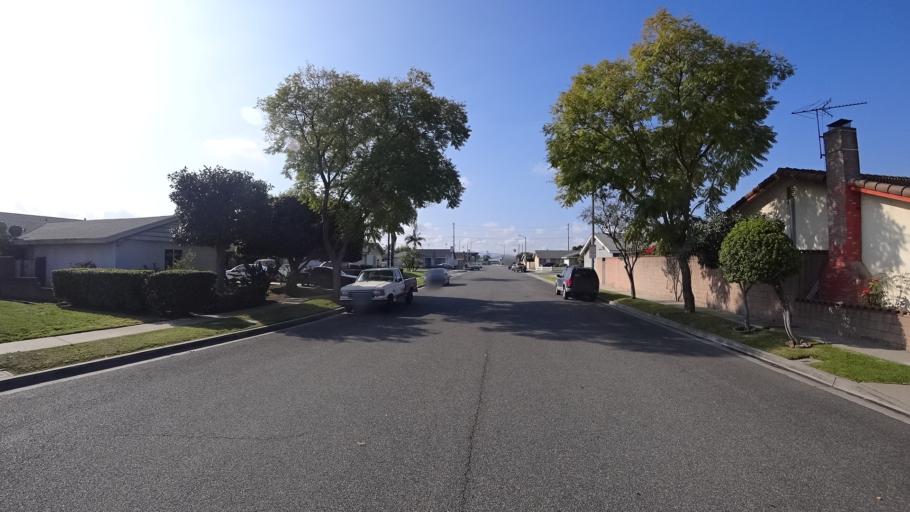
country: US
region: California
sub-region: Los Angeles County
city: Baldwin Park
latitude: 34.0887
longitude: -117.9463
